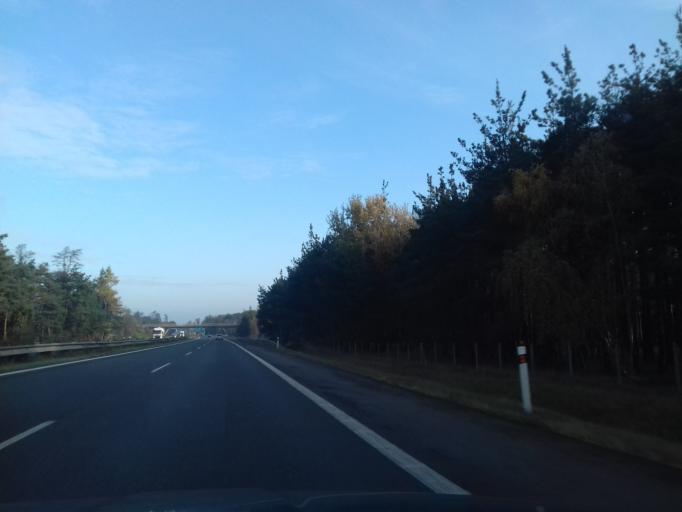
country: SK
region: Bratislavsky
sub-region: Okres Malacky
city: Malacky
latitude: 48.4094
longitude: 17.0354
